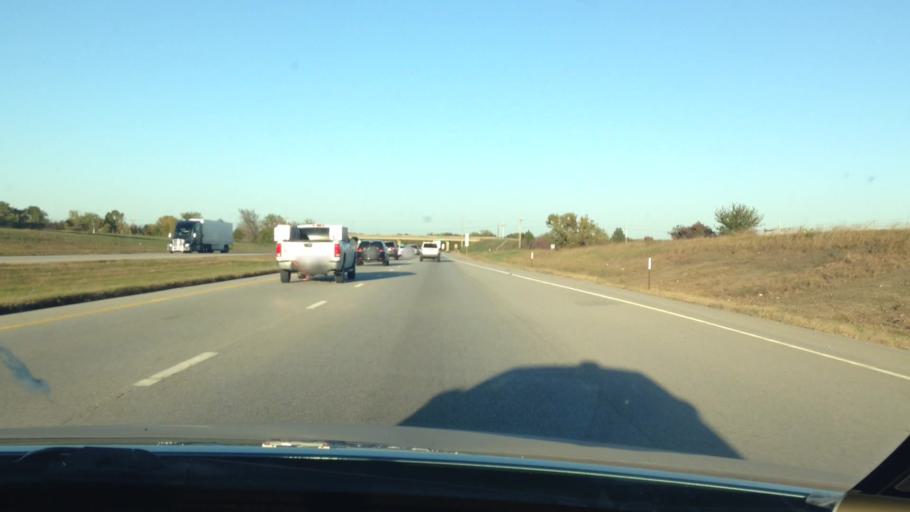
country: US
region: Kansas
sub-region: Johnson County
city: Gardner
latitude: 38.8149
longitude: -94.8756
